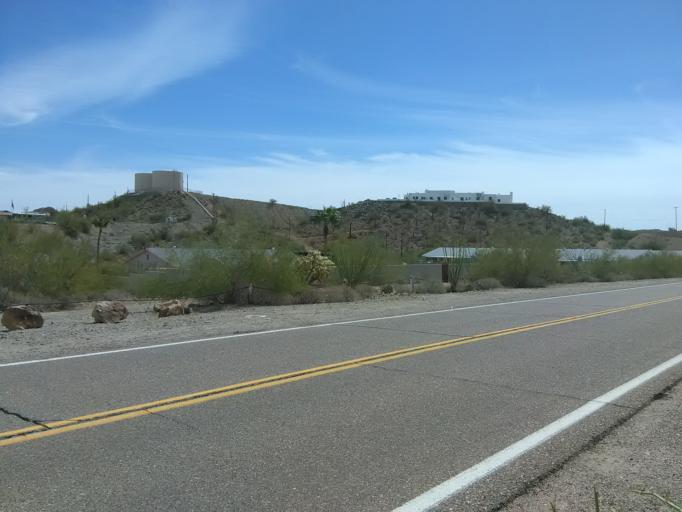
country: US
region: Arizona
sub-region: Pima County
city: Ajo
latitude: 32.3691
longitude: -112.8717
